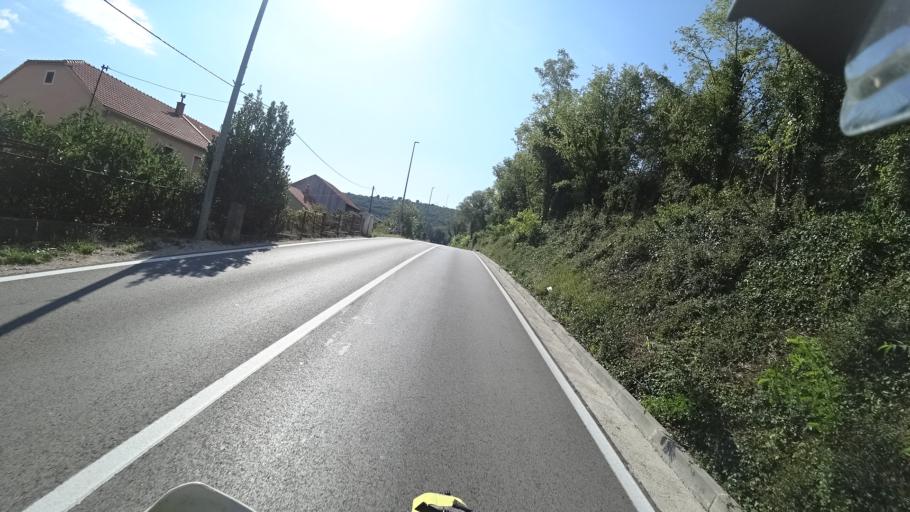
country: HR
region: Sibensko-Kniniska
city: Knin
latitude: 44.0293
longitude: 16.1924
